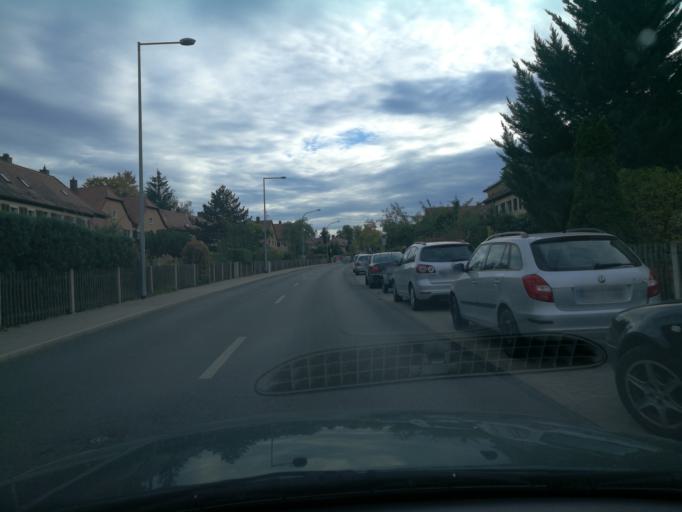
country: DE
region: Bavaria
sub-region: Regierungsbezirk Mittelfranken
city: Furth
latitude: 49.4890
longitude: 10.9747
